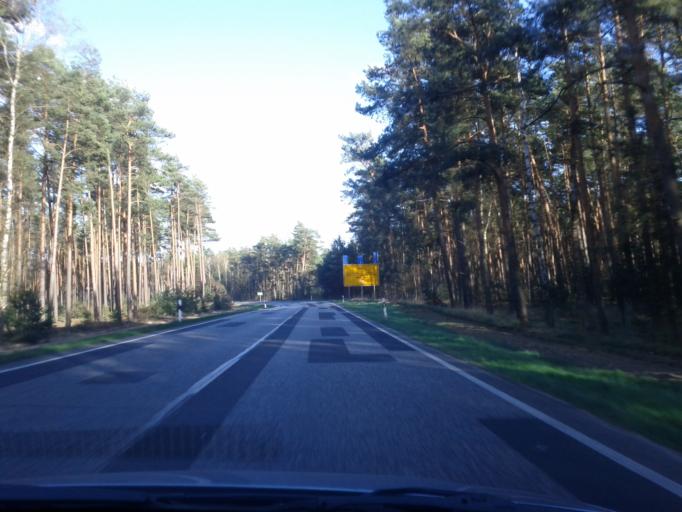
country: DE
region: Brandenburg
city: Grunheide
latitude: 52.3919
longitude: 13.8210
